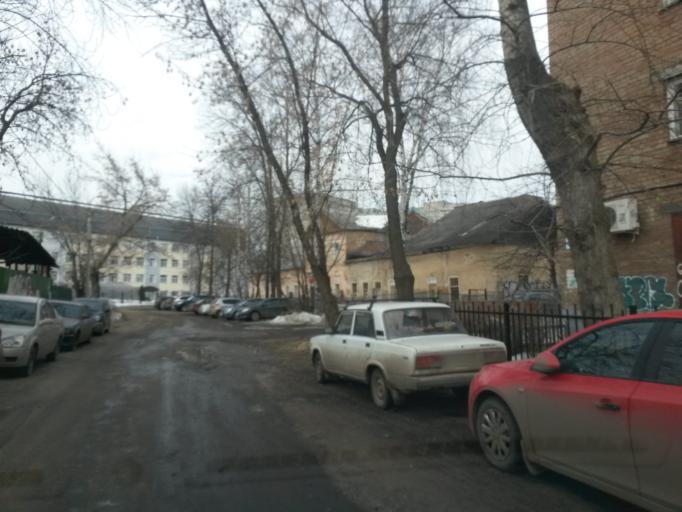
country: RU
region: Jaroslavl
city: Yaroslavl
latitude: 57.6365
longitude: 39.8719
